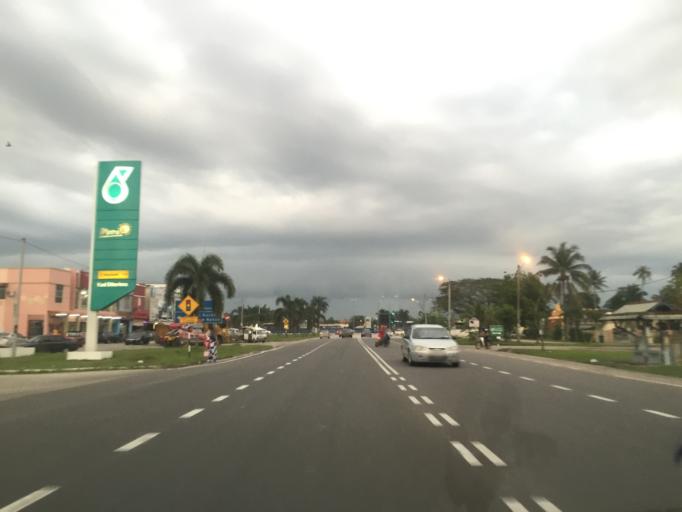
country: MY
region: Penang
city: Tasek Glugor
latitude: 5.5154
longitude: 100.5454
